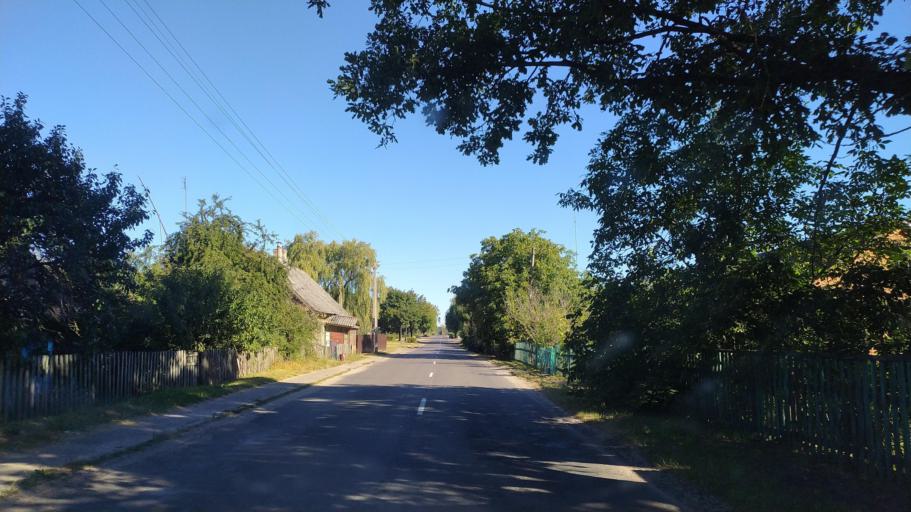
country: BY
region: Brest
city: Pruzhany
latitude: 52.4856
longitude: 24.7075
